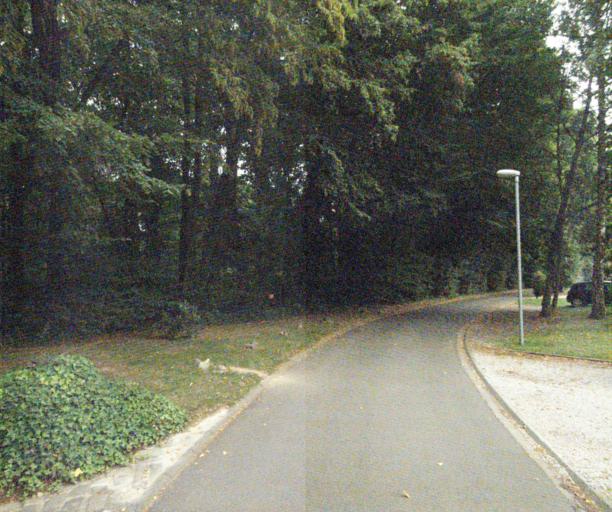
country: FR
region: Nord-Pas-de-Calais
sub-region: Departement du Nord
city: Baisieux
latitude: 50.6136
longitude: 3.2530
